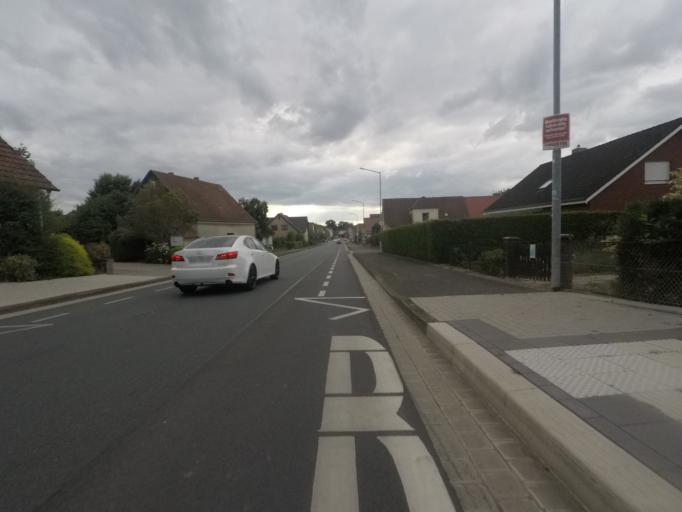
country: DE
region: North Rhine-Westphalia
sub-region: Regierungsbezirk Detmold
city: Hiddenhausen
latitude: 52.1694
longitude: 8.6358
